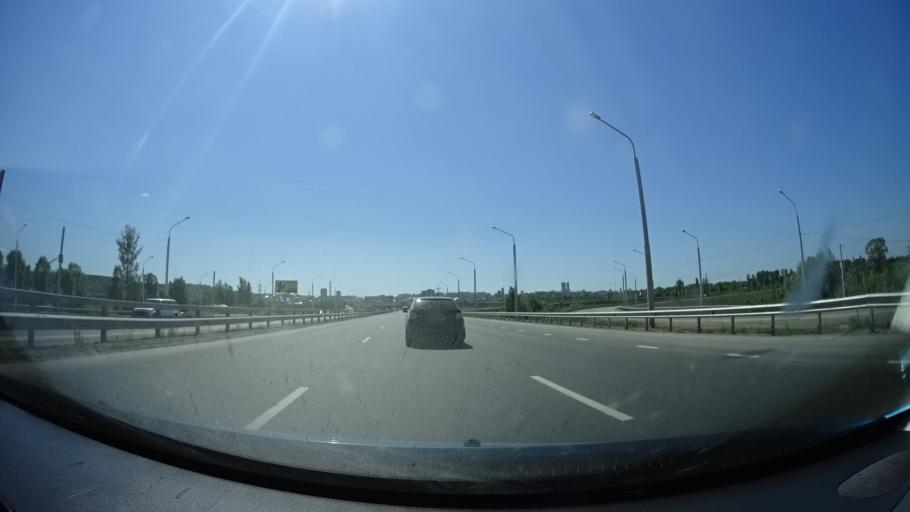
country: RU
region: Bashkortostan
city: Ufa
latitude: 54.7686
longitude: 55.9545
